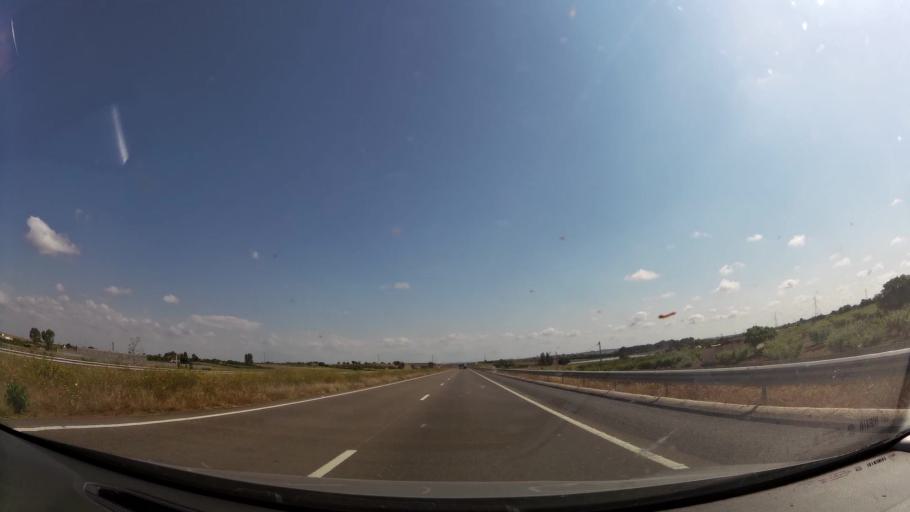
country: MA
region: Rabat-Sale-Zemmour-Zaer
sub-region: Skhirate-Temara
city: Temara
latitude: 33.8895
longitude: -6.7907
